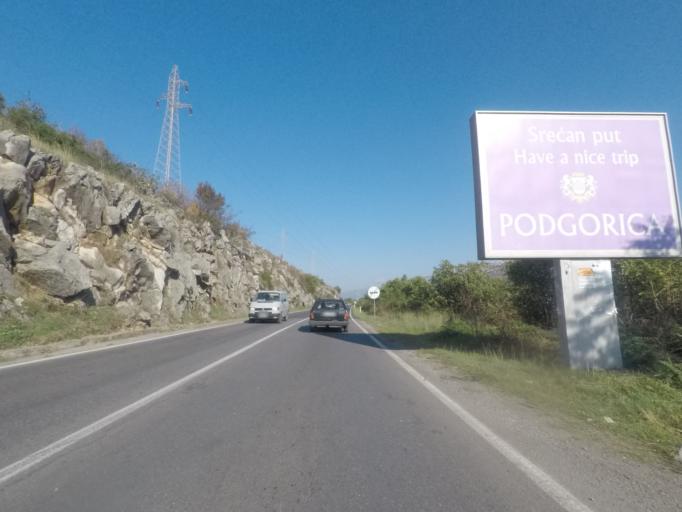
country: ME
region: Podgorica
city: Podgorica
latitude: 42.4454
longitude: 19.2029
